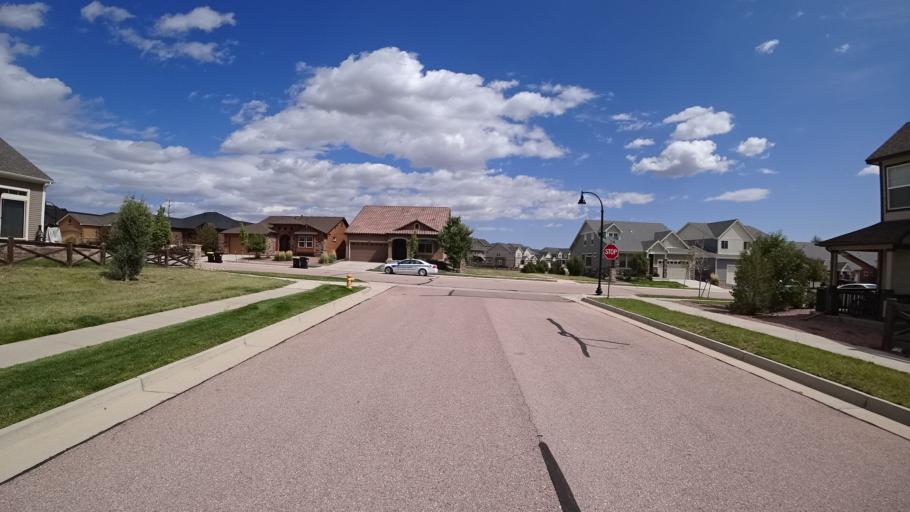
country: US
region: Colorado
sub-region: El Paso County
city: Cimarron Hills
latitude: 38.9357
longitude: -104.6729
